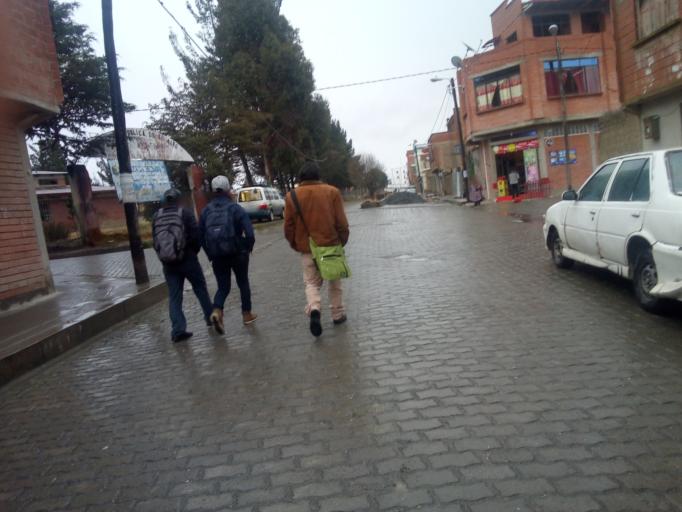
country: BO
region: La Paz
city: Achacachi
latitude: -16.0435
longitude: -68.6894
